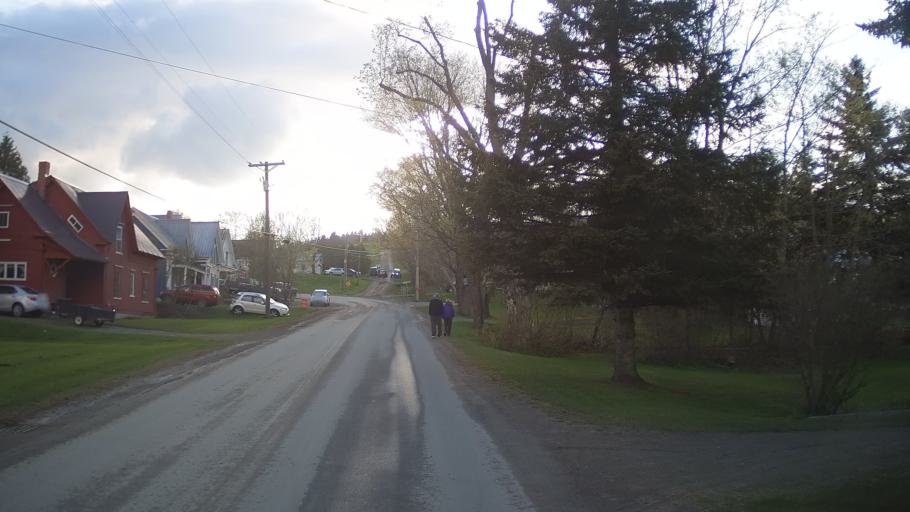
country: US
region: Vermont
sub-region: Orleans County
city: Newport
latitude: 44.7291
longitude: -72.2263
